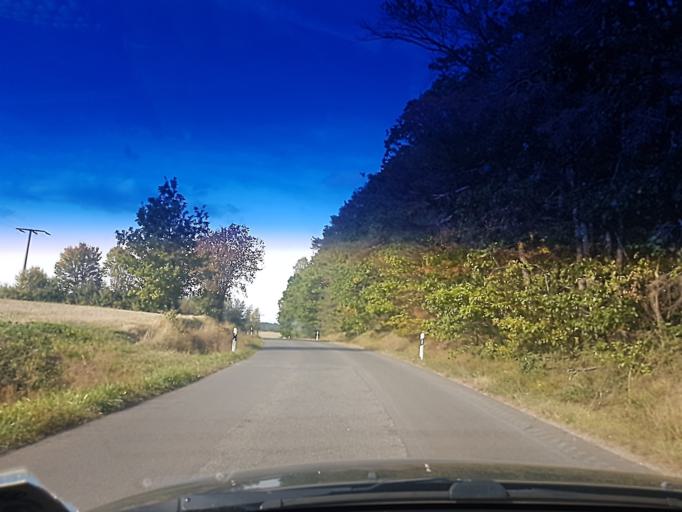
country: DE
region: Bavaria
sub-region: Upper Franconia
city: Schlusselfeld
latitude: 49.7826
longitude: 10.5841
